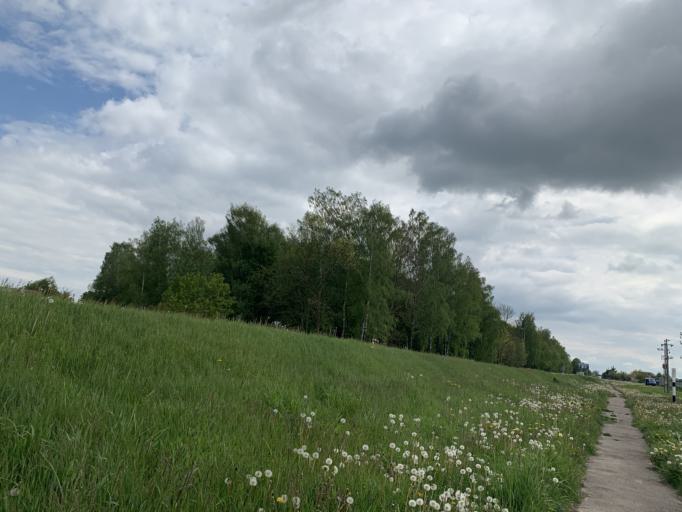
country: BY
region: Minsk
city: Nyasvizh
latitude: 53.2375
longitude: 26.6769
